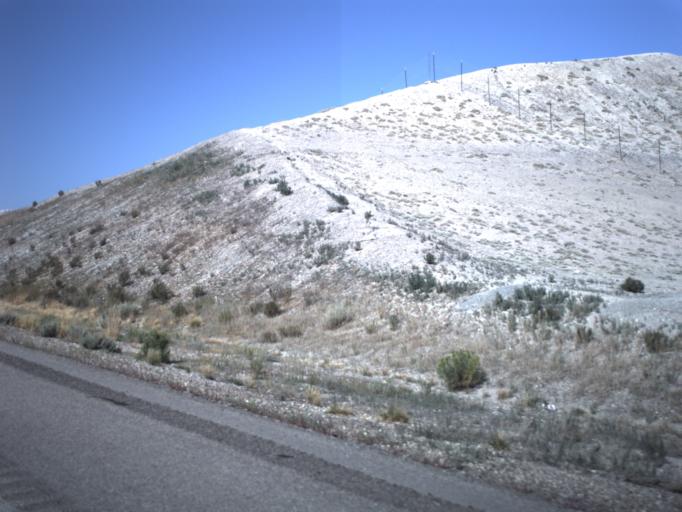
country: US
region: Utah
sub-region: Emery County
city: Ferron
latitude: 38.9517
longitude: -111.2084
